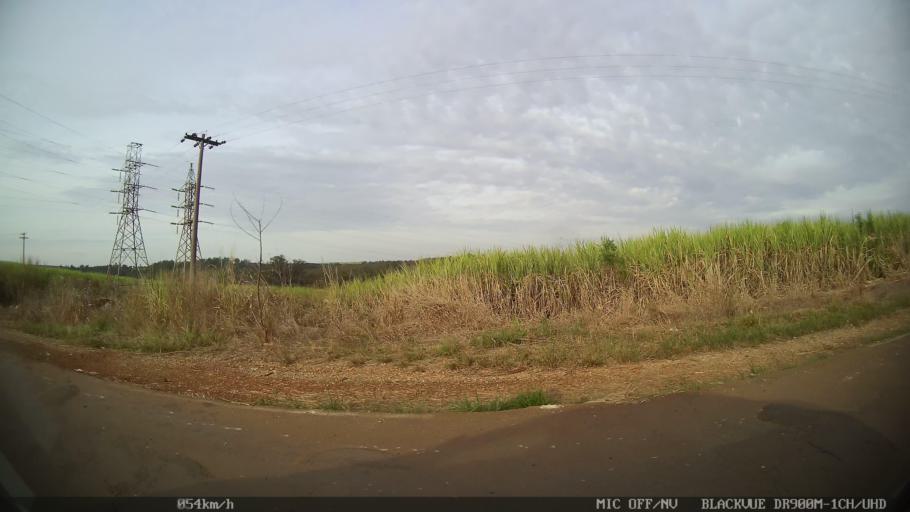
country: BR
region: Sao Paulo
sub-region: Piracicaba
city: Piracicaba
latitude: -22.7112
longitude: -47.5800
